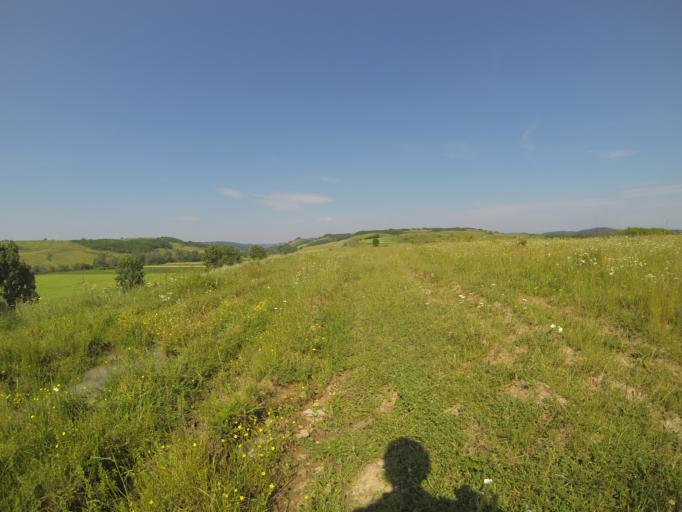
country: RO
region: Gorj
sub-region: Comuna Crusetu
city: Crusetu
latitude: 44.6065
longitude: 23.6768
